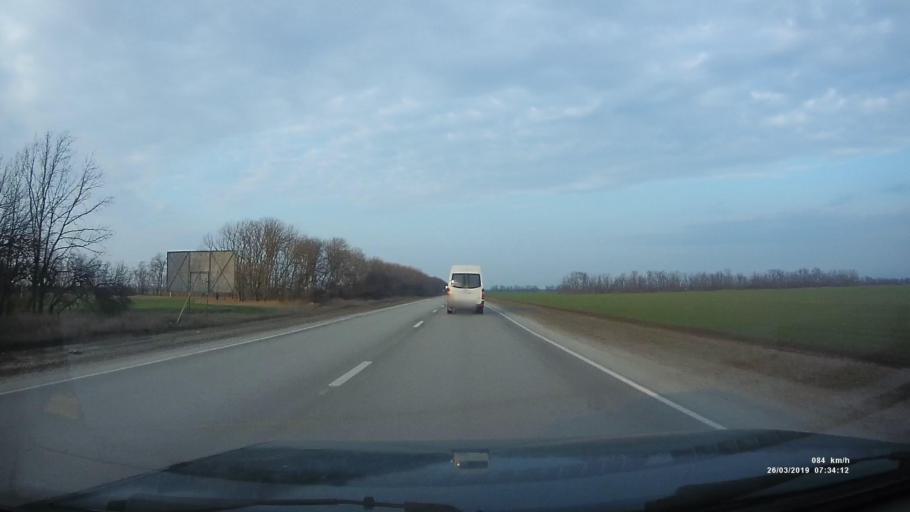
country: RU
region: Rostov
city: Novobessergenovka
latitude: 47.2114
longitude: 38.7605
